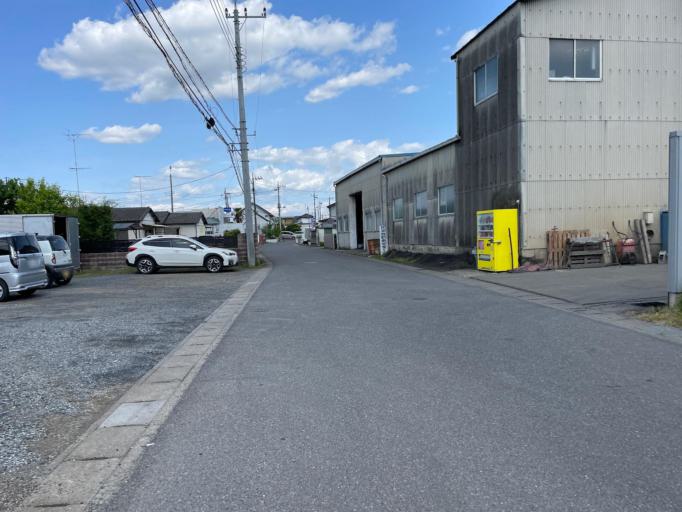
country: JP
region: Tochigi
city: Fujioka
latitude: 36.3199
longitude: 139.6634
